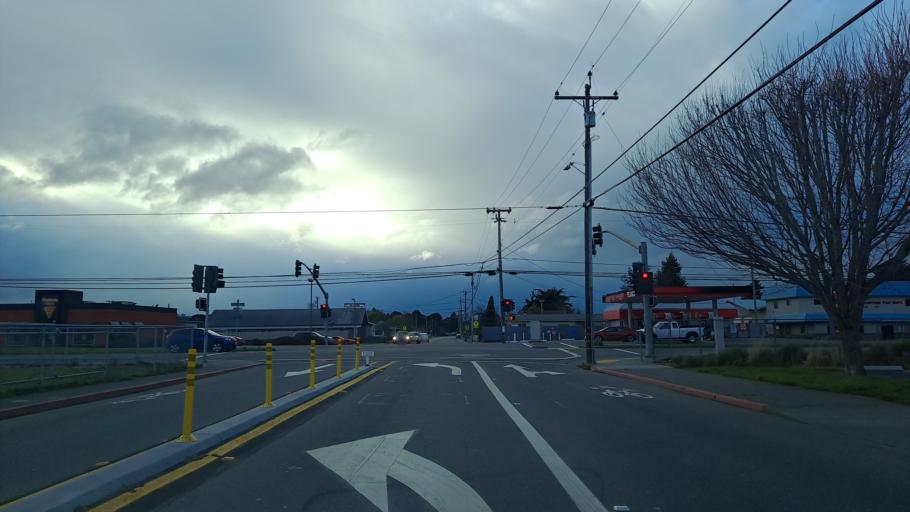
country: US
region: California
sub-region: Humboldt County
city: Fortuna
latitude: 40.5886
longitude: -124.1462
